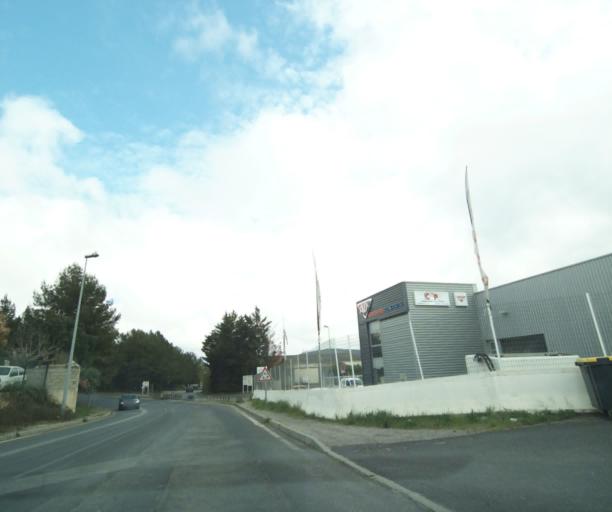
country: FR
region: Languedoc-Roussillon
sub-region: Departement de l'Herault
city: Fabregues
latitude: 43.5585
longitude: 3.7972
